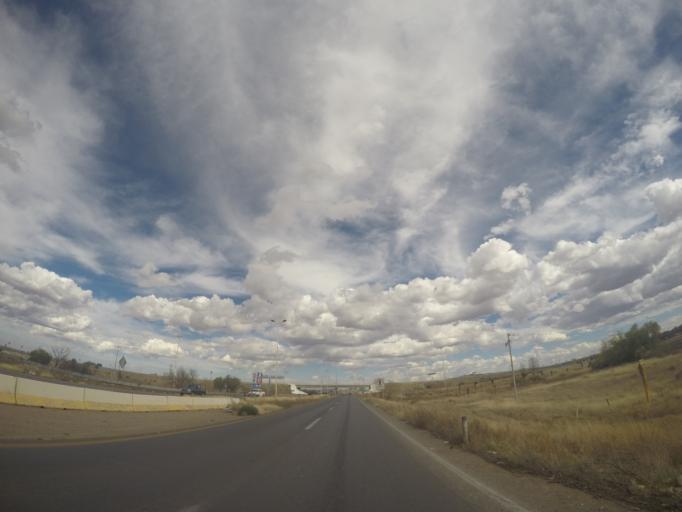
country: MX
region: Zacatecas
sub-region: Guadalupe
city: Martinez Dominguez
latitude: 22.7532
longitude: -102.4540
